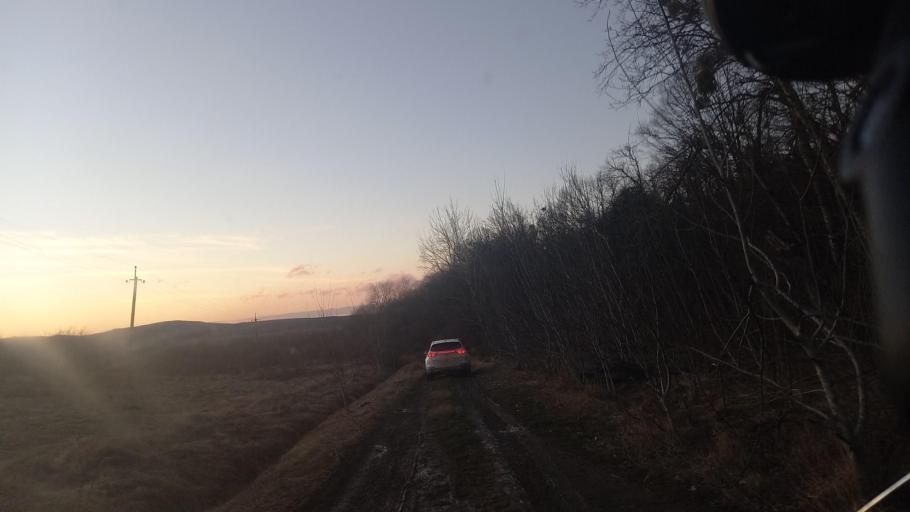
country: RU
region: Krasnodarskiy
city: Smolenskaya
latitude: 44.7259
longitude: 38.8420
